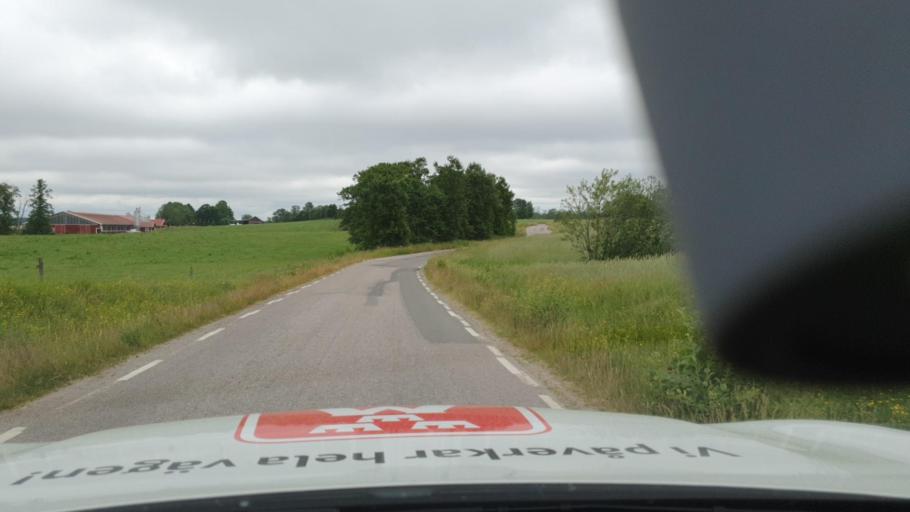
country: SE
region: Vaestra Goetaland
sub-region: Tibro Kommun
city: Tibro
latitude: 58.3767
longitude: 14.1770
